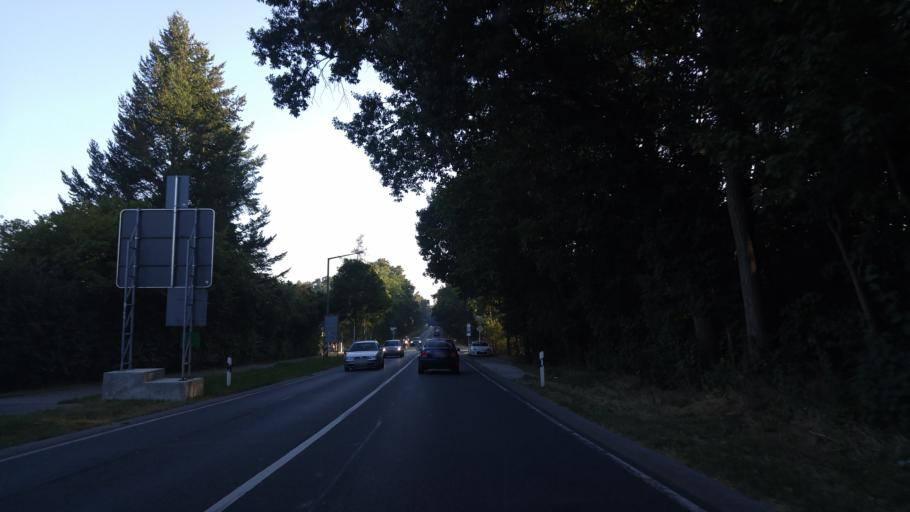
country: DE
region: Bavaria
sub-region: Regierungsbezirk Mittelfranken
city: Furth
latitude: 49.5270
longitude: 10.9786
